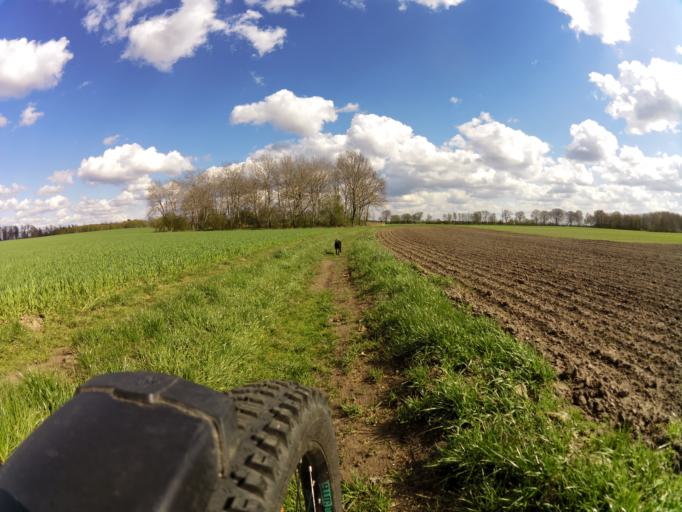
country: PL
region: West Pomeranian Voivodeship
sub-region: Powiat gryficki
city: Ploty
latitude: 53.8338
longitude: 15.2541
